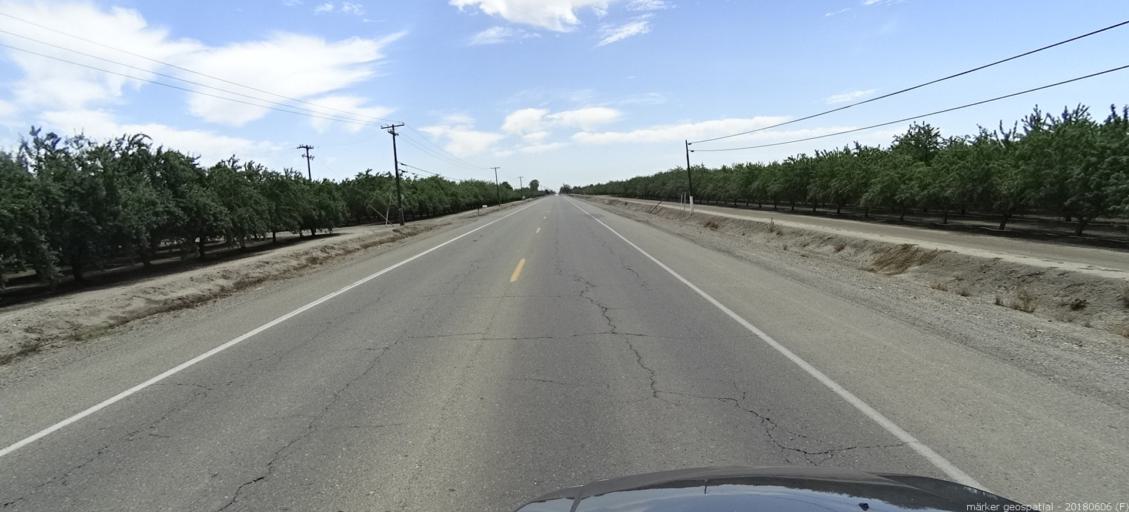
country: US
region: California
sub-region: Fresno County
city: Firebaugh
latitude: 36.8583
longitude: -120.4315
